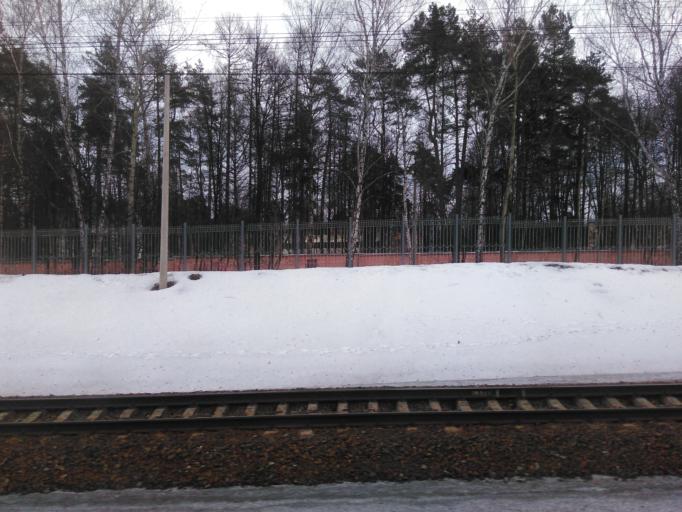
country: RU
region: Moskovskaya
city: Mamontovka
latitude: 55.9894
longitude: 37.8259
